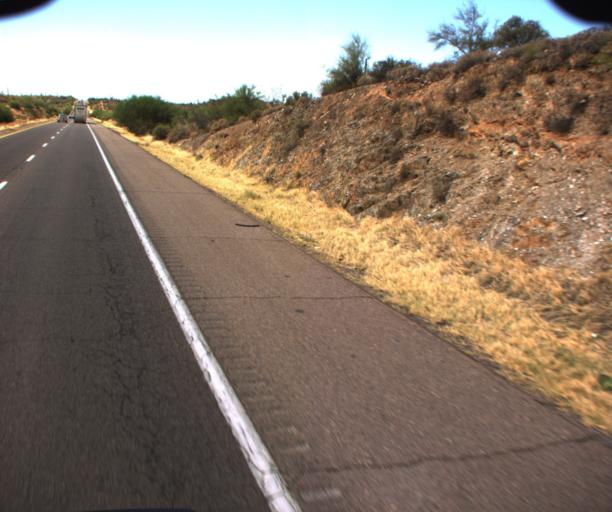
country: US
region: Arizona
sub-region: Maricopa County
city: New River
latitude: 33.9453
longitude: -112.1405
